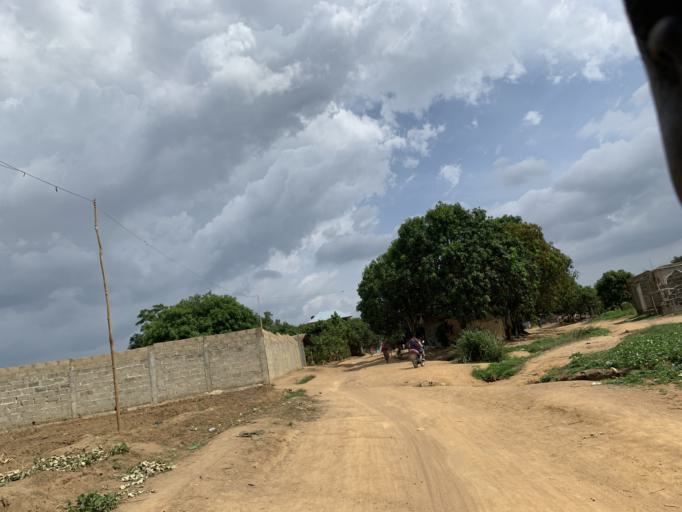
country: SL
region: Western Area
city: Waterloo
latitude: 8.3429
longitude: -13.0528
